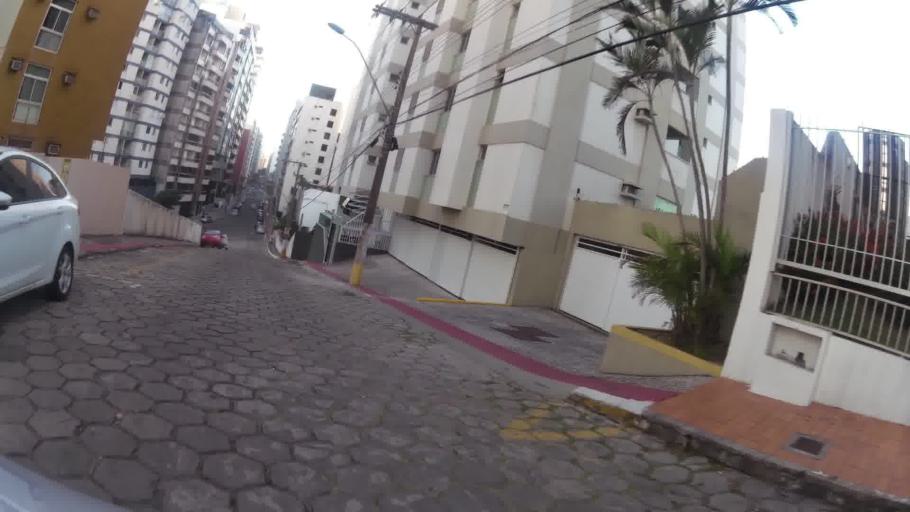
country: BR
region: Espirito Santo
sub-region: Guarapari
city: Guarapari
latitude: -20.6757
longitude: -40.5019
